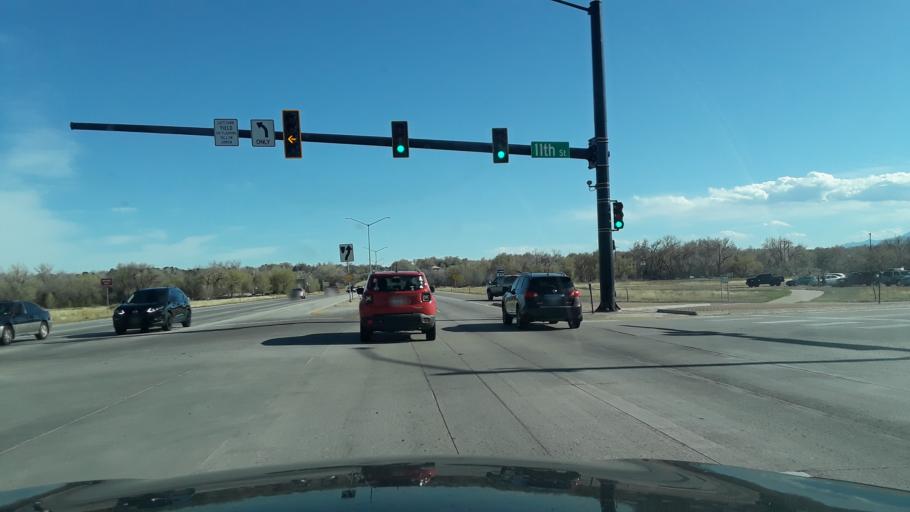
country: US
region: Colorado
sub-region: Pueblo County
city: Pueblo
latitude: 38.2770
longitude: -104.6629
